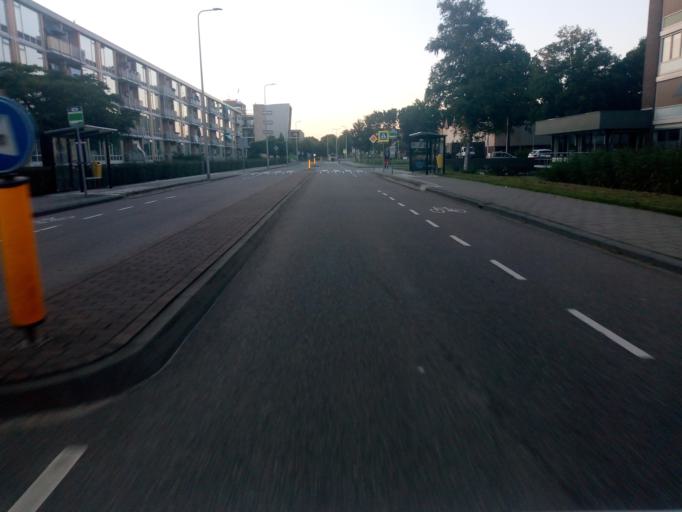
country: NL
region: South Holland
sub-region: Gemeente Alphen aan den Rijn
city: Alphen aan den Rijn
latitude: 52.1324
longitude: 4.6510
